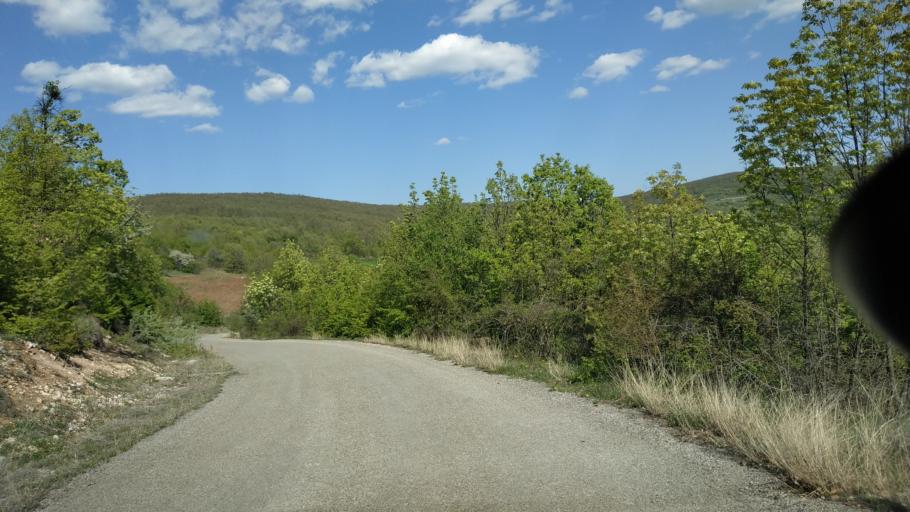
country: RS
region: Central Serbia
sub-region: Zajecarski Okrug
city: Soko Banja
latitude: 43.4988
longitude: 21.8824
